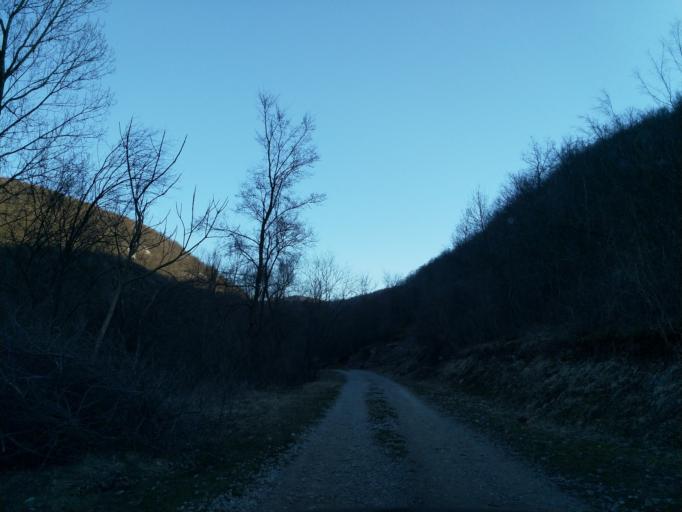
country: RS
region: Central Serbia
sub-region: Pomoravski Okrug
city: Paracin
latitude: 43.9284
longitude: 21.5231
